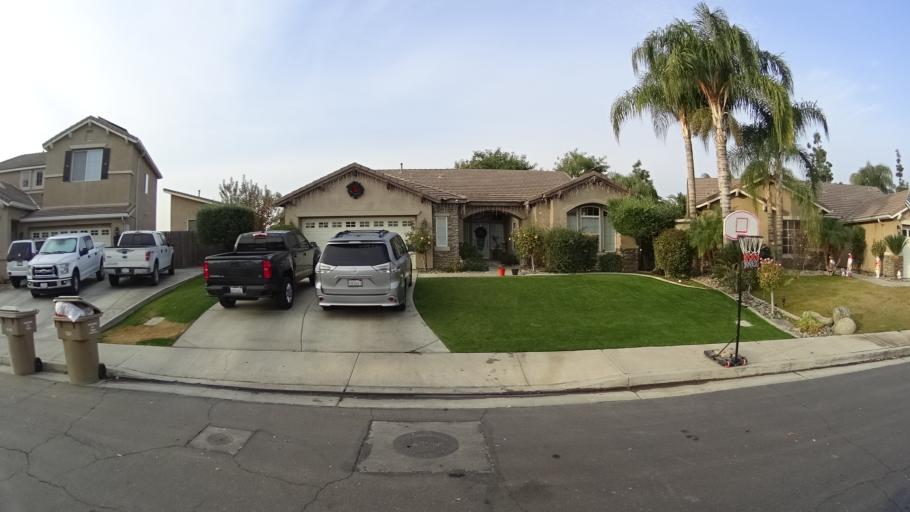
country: US
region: California
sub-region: Kern County
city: Greenacres
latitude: 35.4203
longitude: -119.1245
